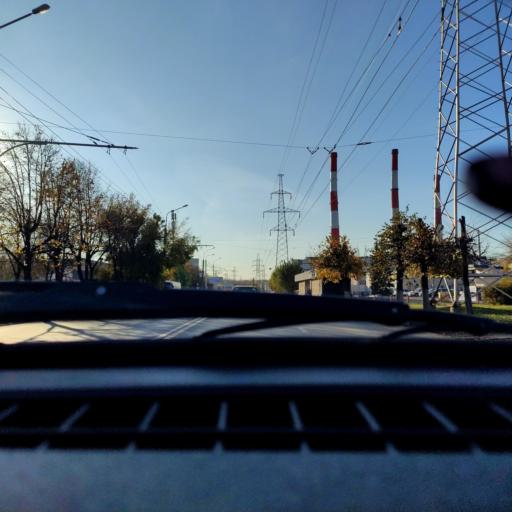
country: RU
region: Bashkortostan
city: Ufa
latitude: 54.7881
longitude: 56.1290
